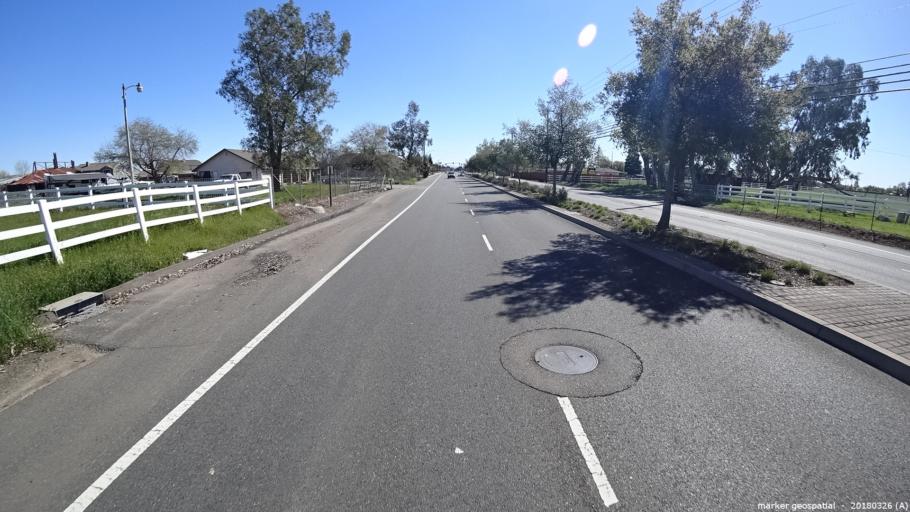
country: US
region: California
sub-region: Sacramento County
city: Vineyard
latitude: 38.4527
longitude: -121.3285
